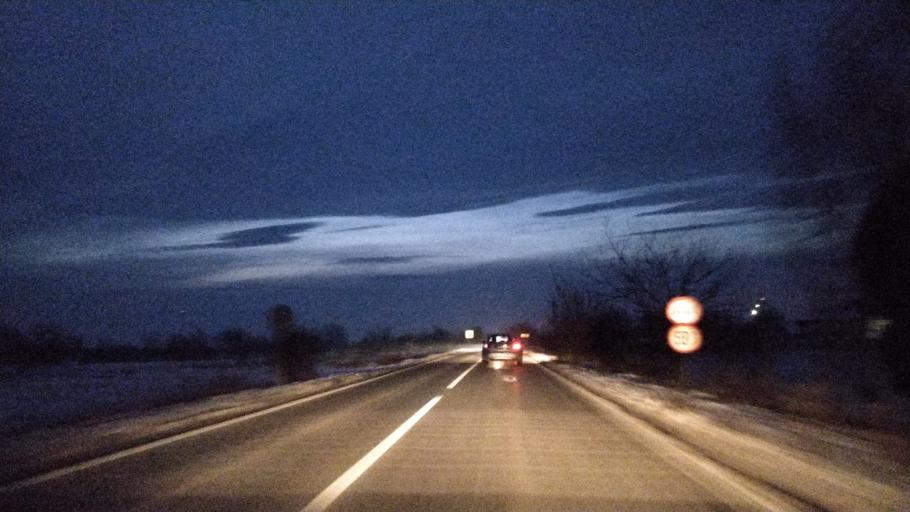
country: RO
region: Vrancea
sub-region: Comuna Milcovul
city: Milcovul
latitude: 45.6777
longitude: 27.2383
